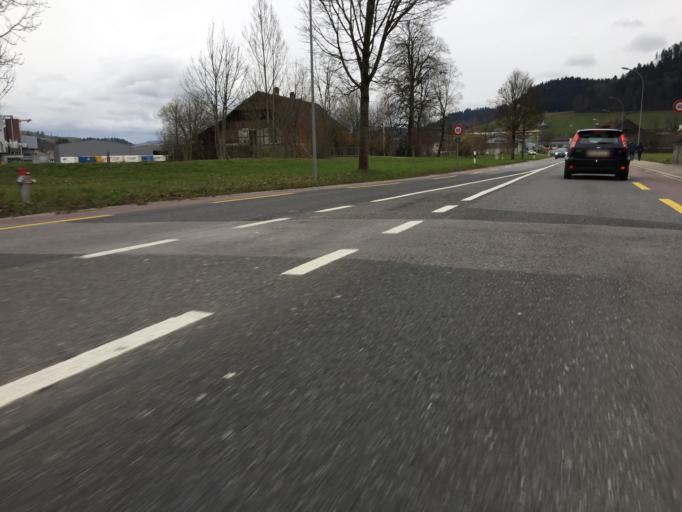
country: CH
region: Bern
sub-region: Emmental District
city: Oberburg
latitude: 47.0442
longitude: 7.6225
